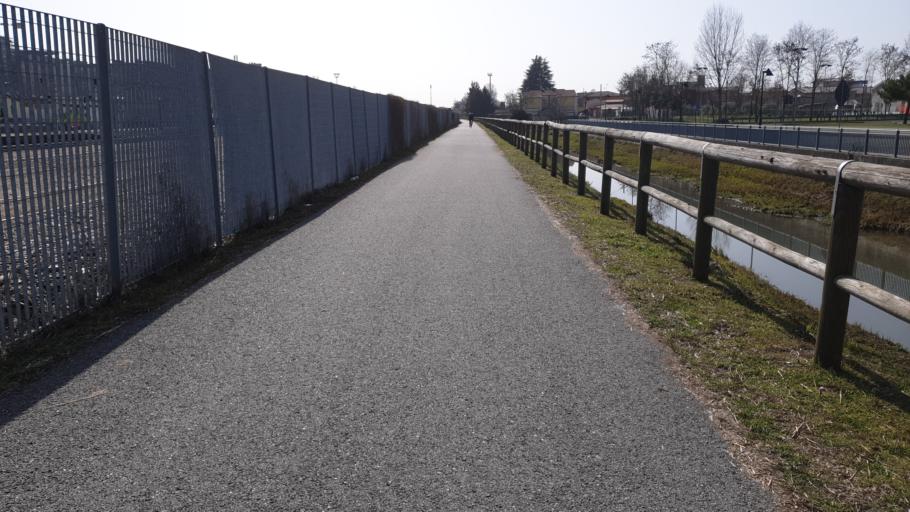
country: IT
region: Veneto
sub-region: Provincia di Padova
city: Camposampiero
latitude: 45.5686
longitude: 11.9276
